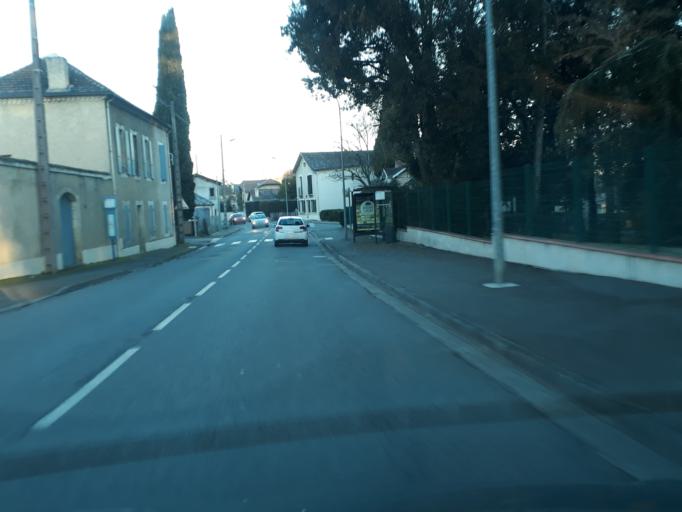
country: FR
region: Midi-Pyrenees
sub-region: Departement du Gers
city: Auch
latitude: 43.6394
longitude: 0.5990
